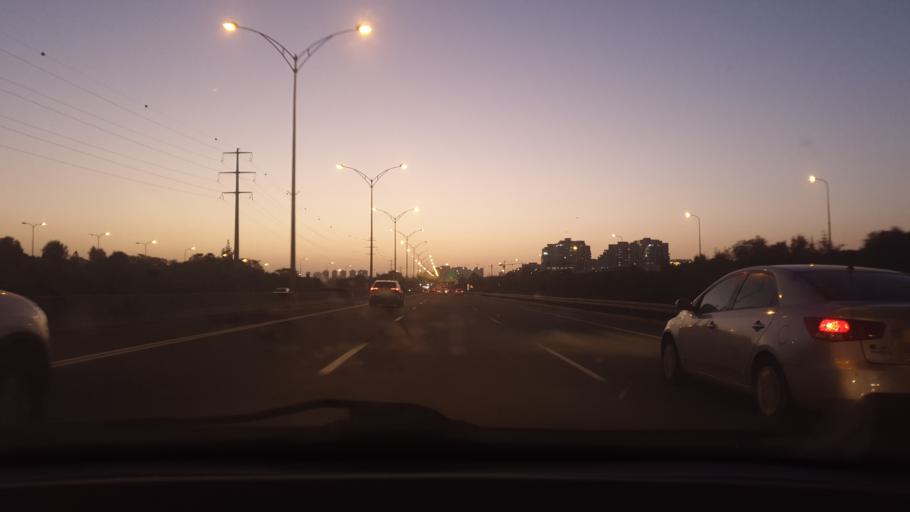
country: IL
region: Central District
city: Nehalim
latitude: 32.0678
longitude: 34.9201
